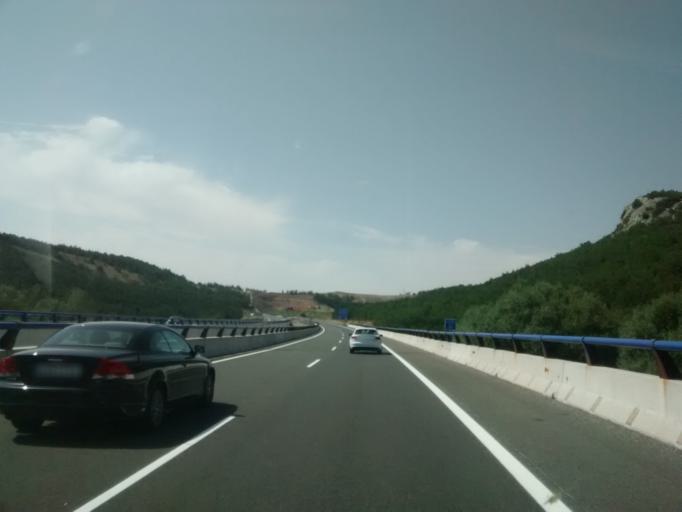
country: ES
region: Castille and Leon
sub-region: Provincia de Palencia
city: Alar del Rey
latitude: 42.6947
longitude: -4.2982
